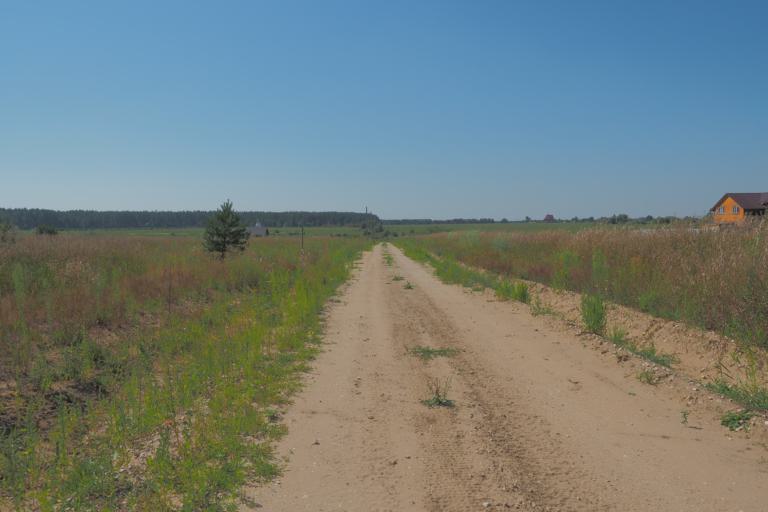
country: RU
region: Moskovskaya
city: Malyshevo
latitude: 55.5372
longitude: 38.3469
